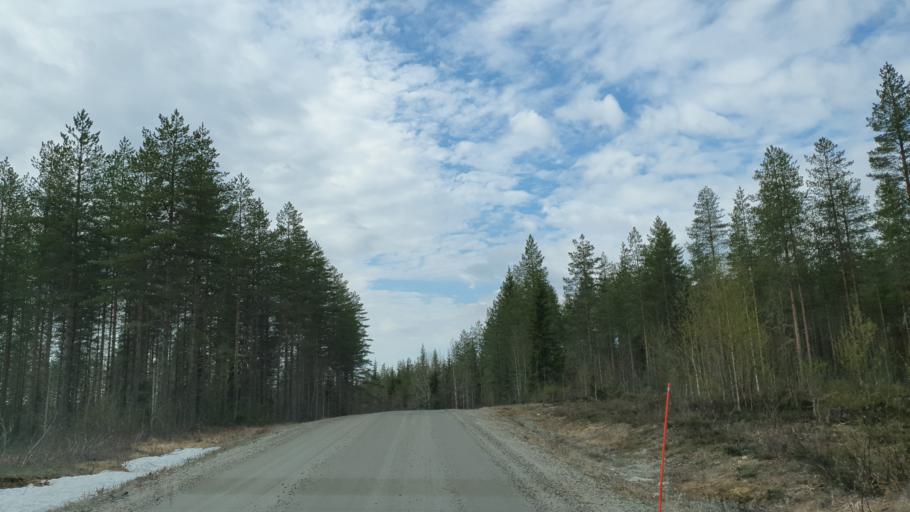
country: FI
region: Kainuu
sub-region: Kehys-Kainuu
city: Kuhmo
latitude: 64.0976
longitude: 29.9215
